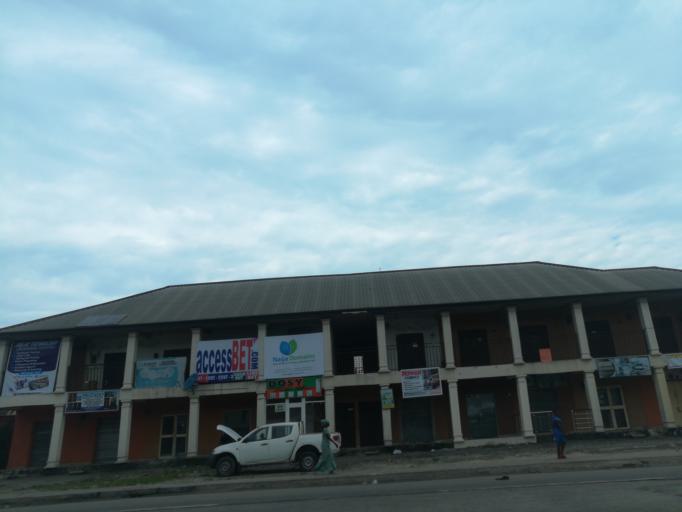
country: NG
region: Rivers
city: Port Harcourt
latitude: 4.8374
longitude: 6.9761
